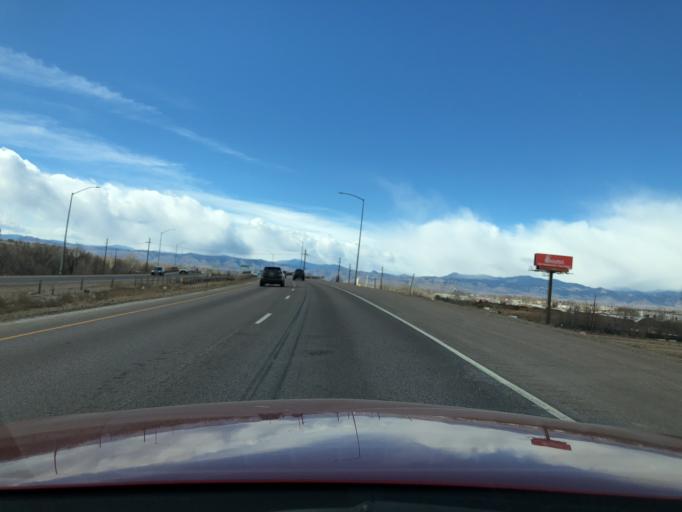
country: US
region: Colorado
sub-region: Adams County
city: Berkley
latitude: 39.7989
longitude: -105.0409
